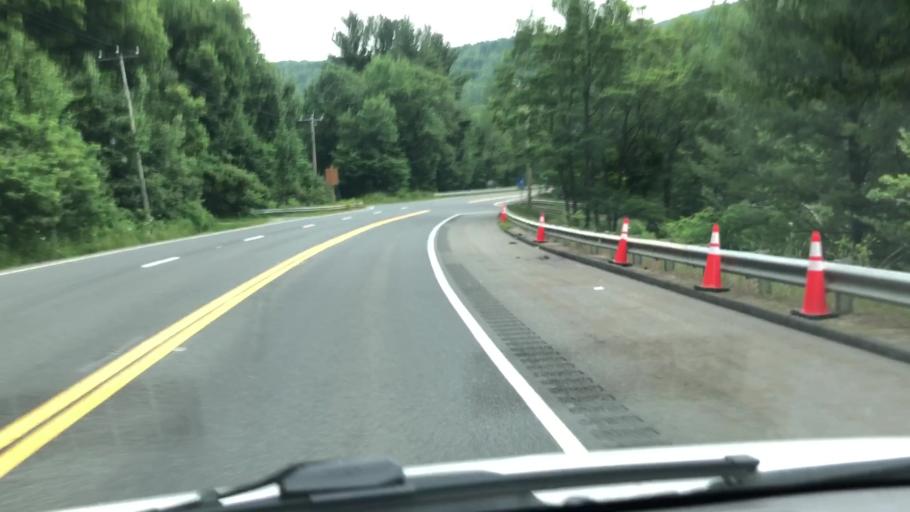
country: US
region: Massachusetts
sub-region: Berkshire County
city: Hinsdale
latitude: 42.4892
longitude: -72.9783
